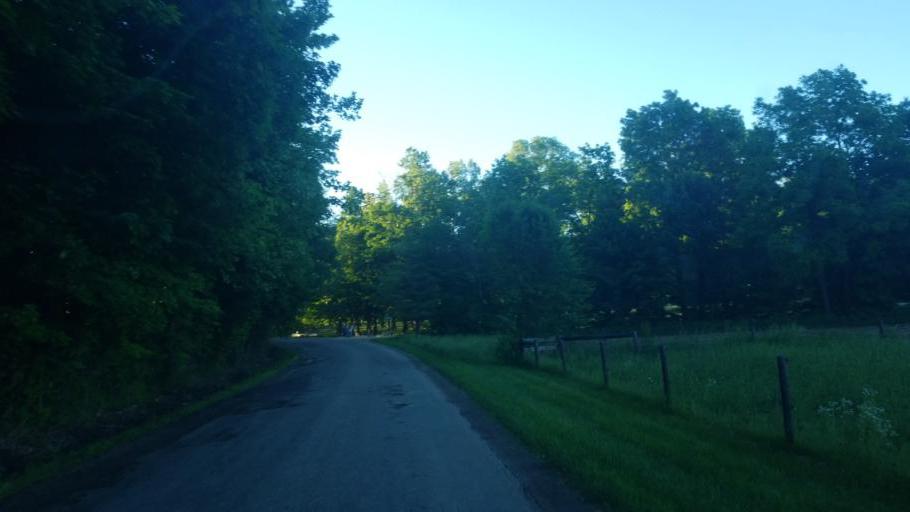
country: US
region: Indiana
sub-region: Elkhart County
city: Nappanee
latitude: 41.4347
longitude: -86.0493
